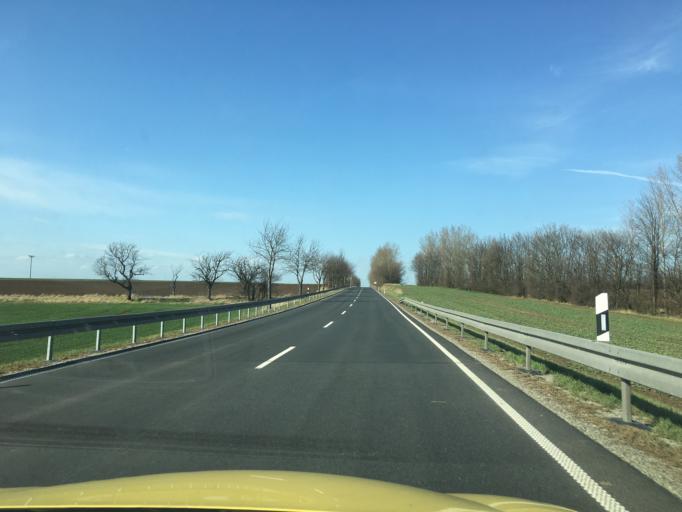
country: DE
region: Thuringia
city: Buttelstedt
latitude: 51.0962
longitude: 11.3499
